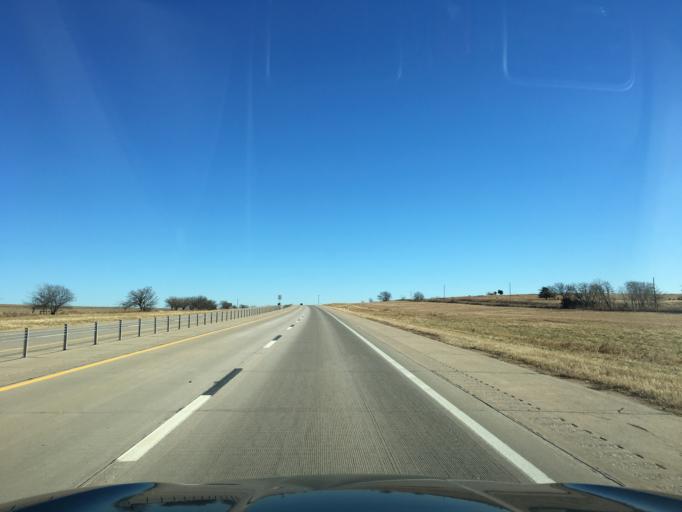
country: US
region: Oklahoma
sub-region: Noble County
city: Perry
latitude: 36.3922
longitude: -97.1862
